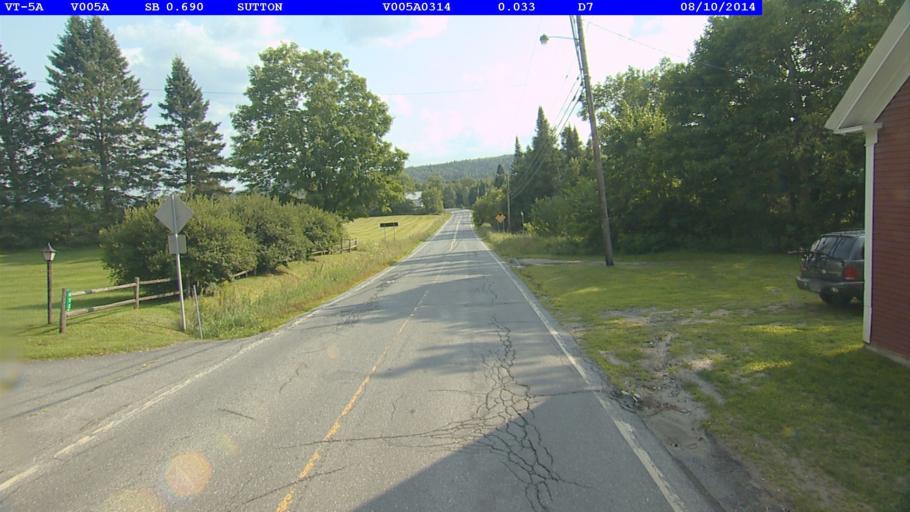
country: US
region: Vermont
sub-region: Caledonia County
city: Lyndonville
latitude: 44.6507
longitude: -71.9818
